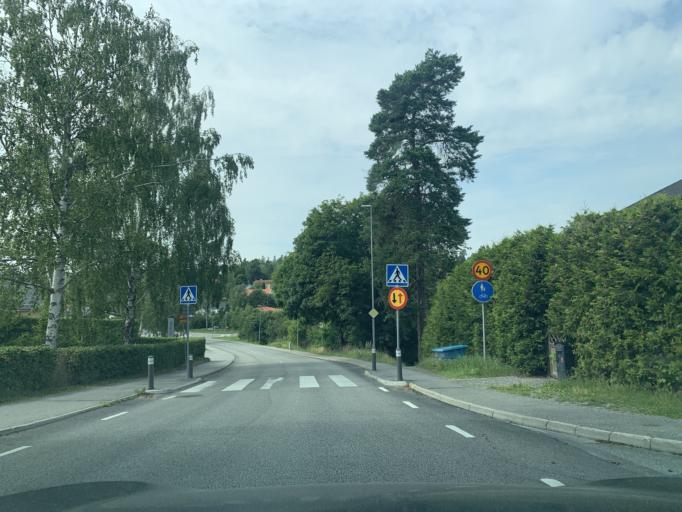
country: SE
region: Stockholm
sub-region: Norrtalje Kommun
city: Bergshamra
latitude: 59.4030
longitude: 18.0214
